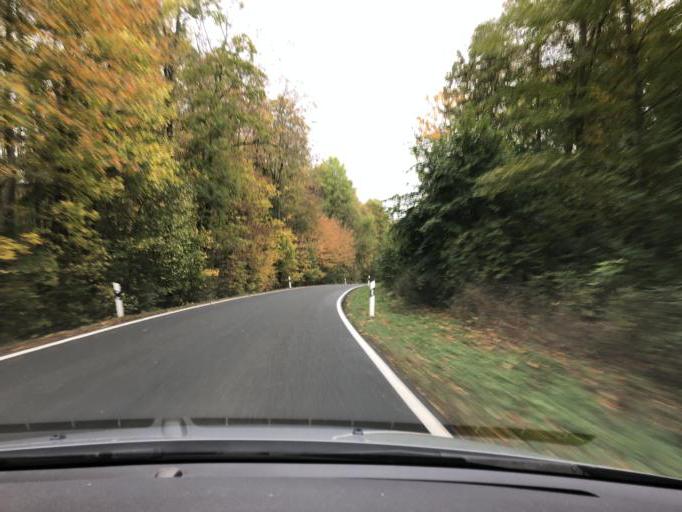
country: DE
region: Thuringia
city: Helmsdorf
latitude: 51.2776
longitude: 10.3574
